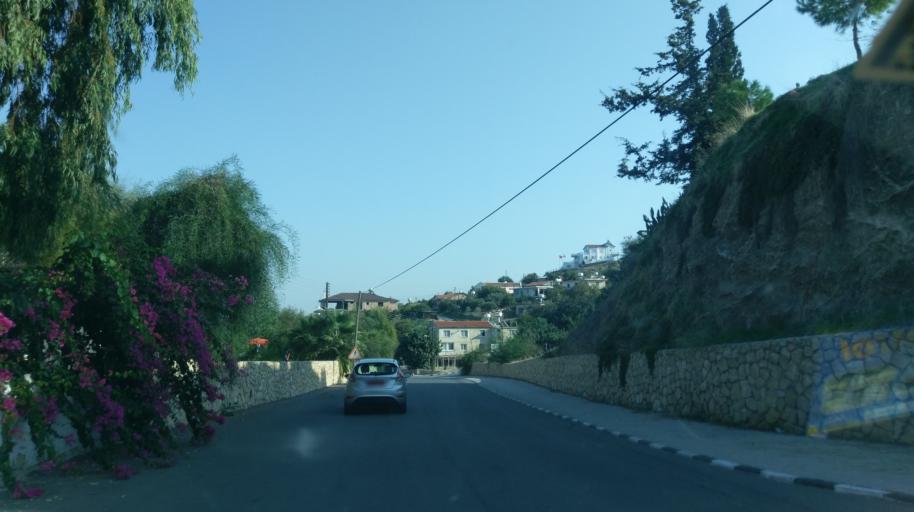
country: CY
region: Lefkosia
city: Lefka
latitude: 35.1495
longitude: 32.7992
